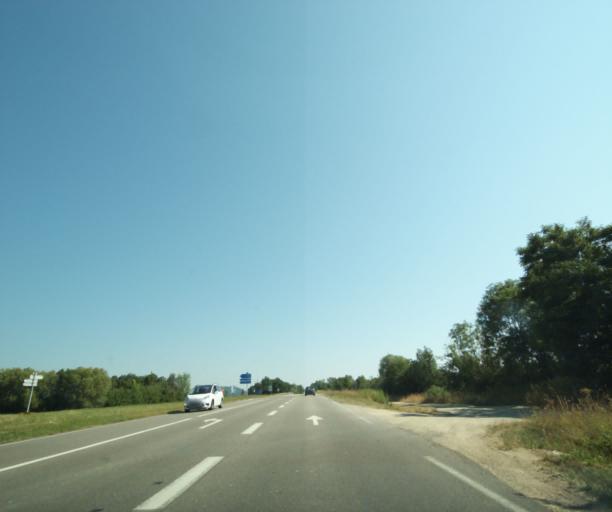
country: FR
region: Lorraine
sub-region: Departement de Meurthe-et-Moselle
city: Ecrouves
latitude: 48.6477
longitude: 5.8689
